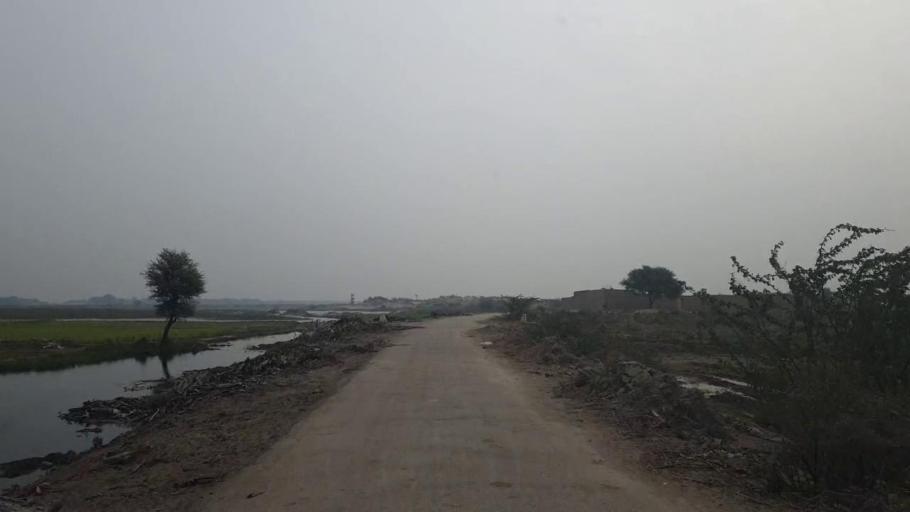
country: PK
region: Sindh
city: Tando Adam
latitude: 25.7526
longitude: 68.6765
